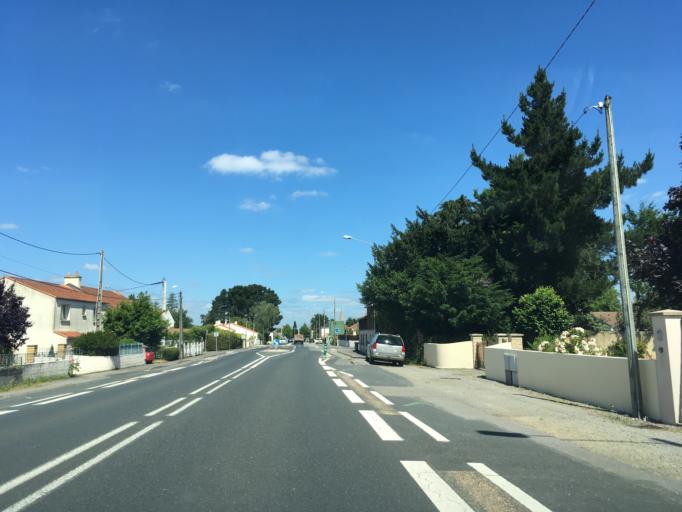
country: FR
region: Pays de la Loire
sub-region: Departement de la Loire-Atlantique
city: Les Sorinieres
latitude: 47.1431
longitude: -1.5247
